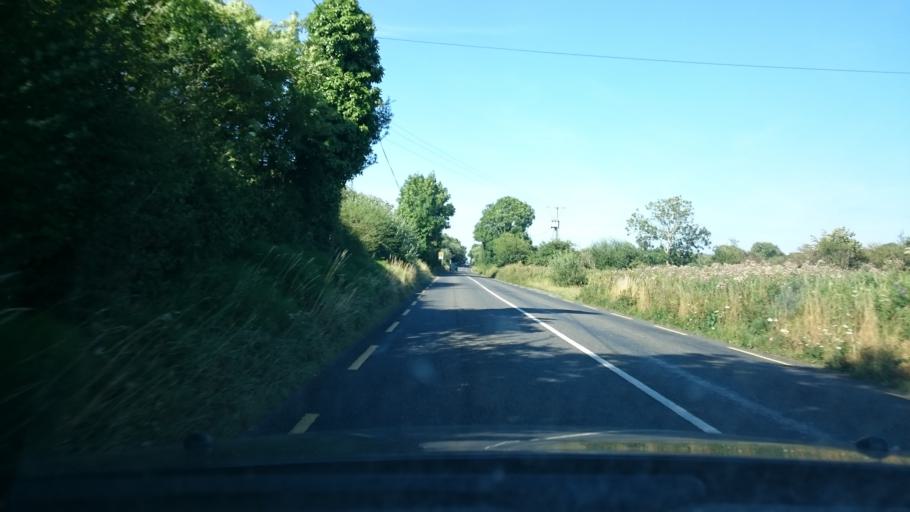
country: IE
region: Leinster
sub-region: Kilkenny
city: Graiguenamanagh
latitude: 52.5548
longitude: -6.9559
